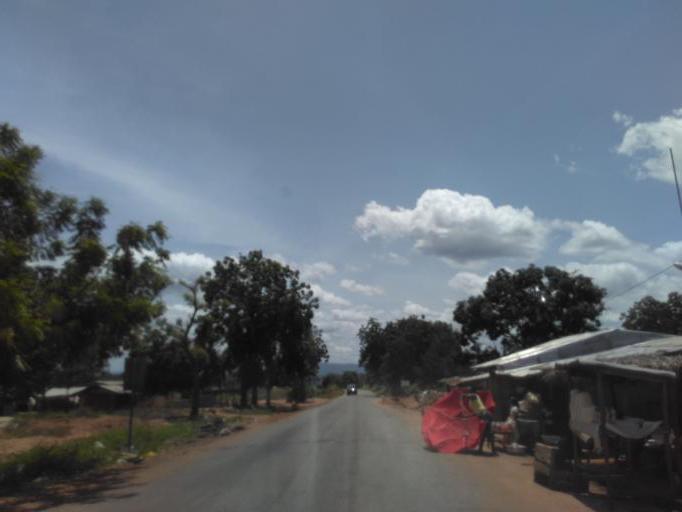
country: GH
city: Akropong
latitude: 6.0661
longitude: -0.0990
